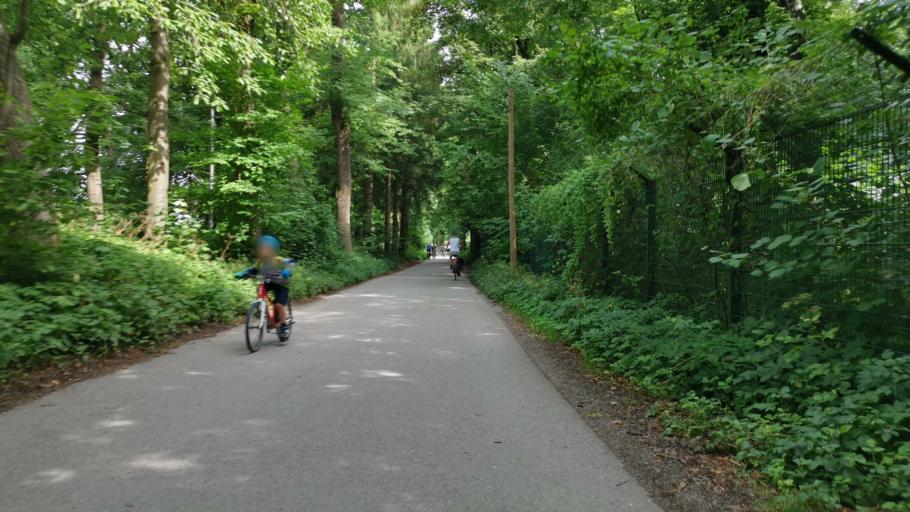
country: DE
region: Bavaria
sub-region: Upper Bavaria
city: Munich
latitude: 48.0980
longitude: 11.5511
